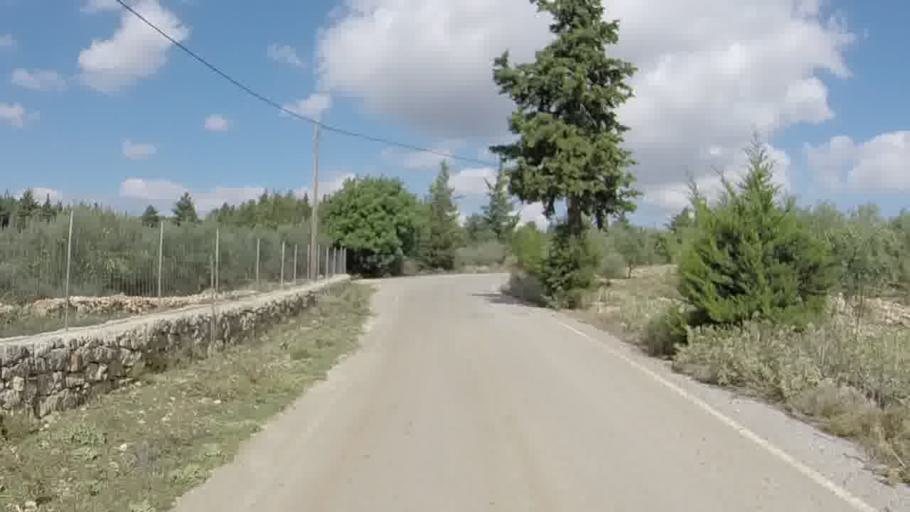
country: GR
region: Crete
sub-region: Nomos Chanias
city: Kalivai
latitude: 35.3897
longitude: 24.1276
